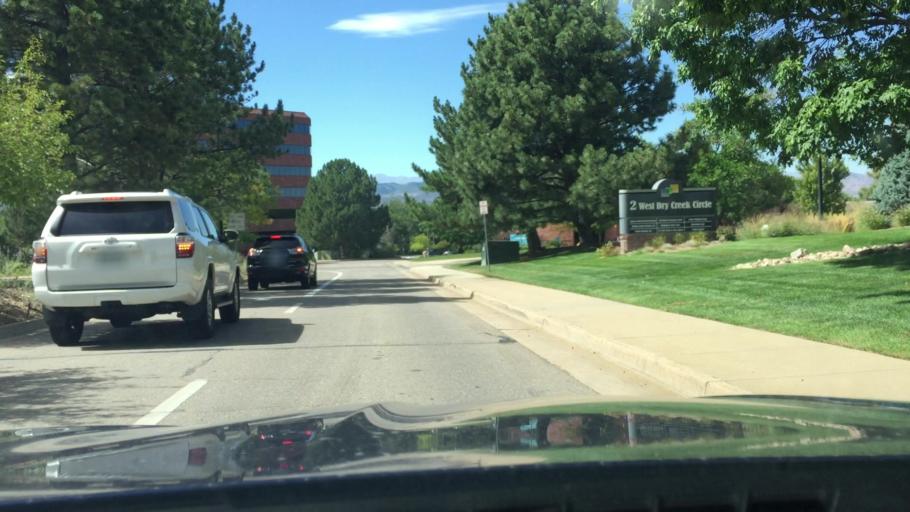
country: US
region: Colorado
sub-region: Douglas County
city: Highlands Ranch
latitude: 39.5807
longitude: -104.9891
